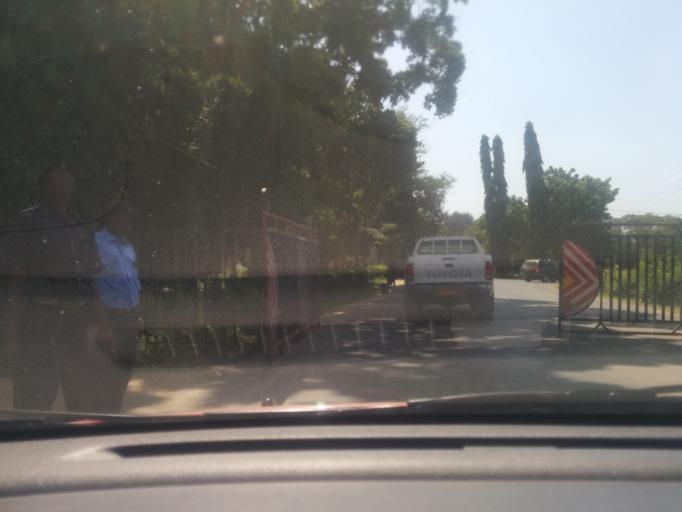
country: TZ
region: Dar es Salaam
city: Magomeni
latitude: -6.7679
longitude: 39.2142
